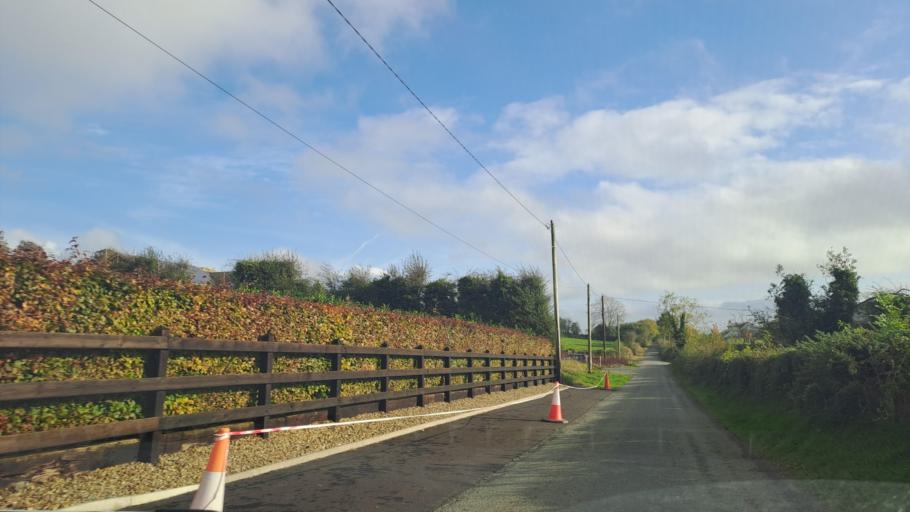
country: IE
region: Ulster
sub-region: County Monaghan
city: Carrickmacross
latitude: 54.0164
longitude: -6.7582
